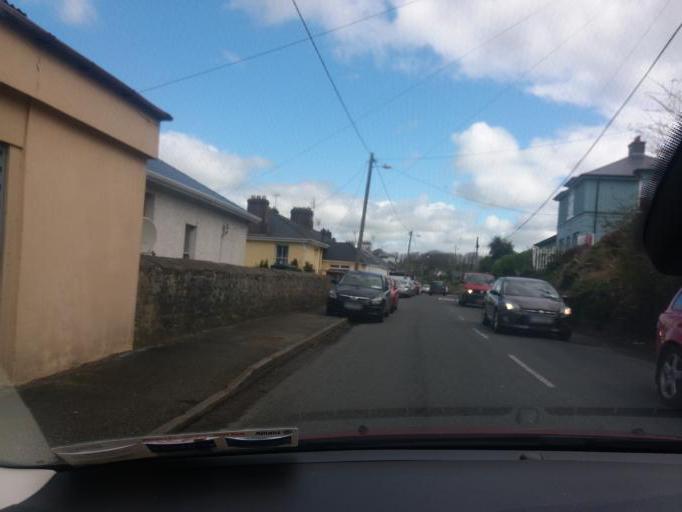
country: IE
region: Munster
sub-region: County Cork
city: Passage West
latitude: 51.8687
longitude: -8.3247
